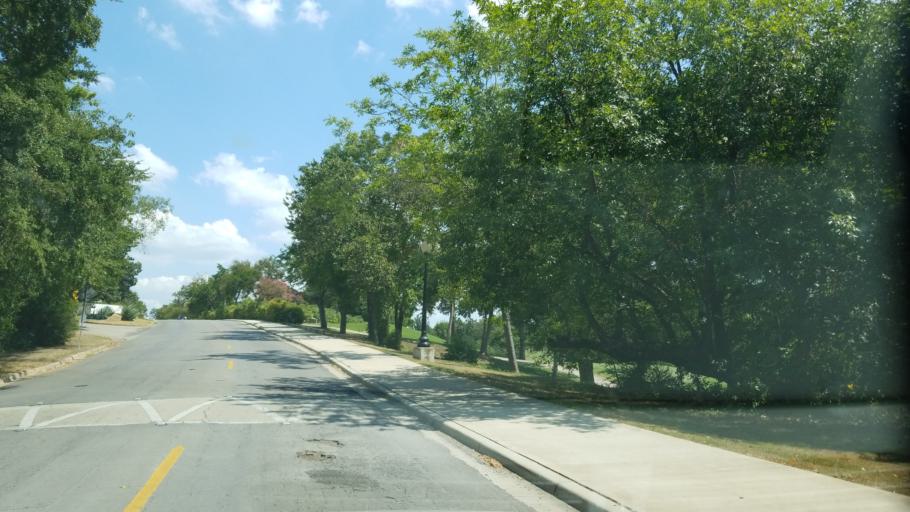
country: US
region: Texas
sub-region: Dallas County
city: Cockrell Hill
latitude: 32.7564
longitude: -96.8543
